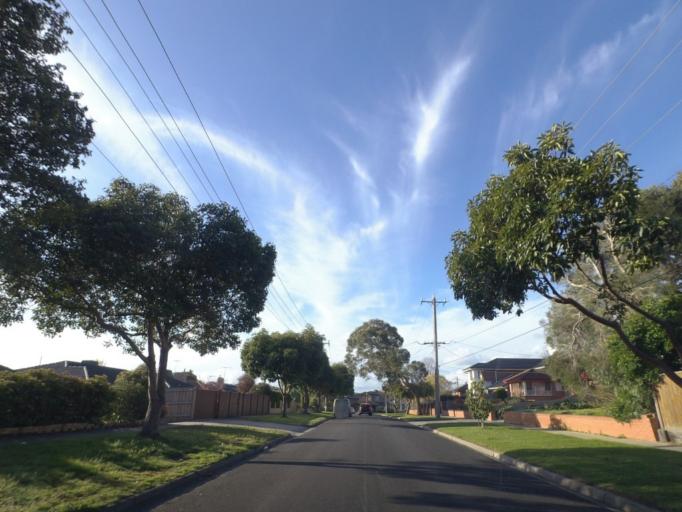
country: AU
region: Victoria
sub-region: Whitehorse
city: Box Hill North
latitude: -37.8002
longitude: 145.1342
